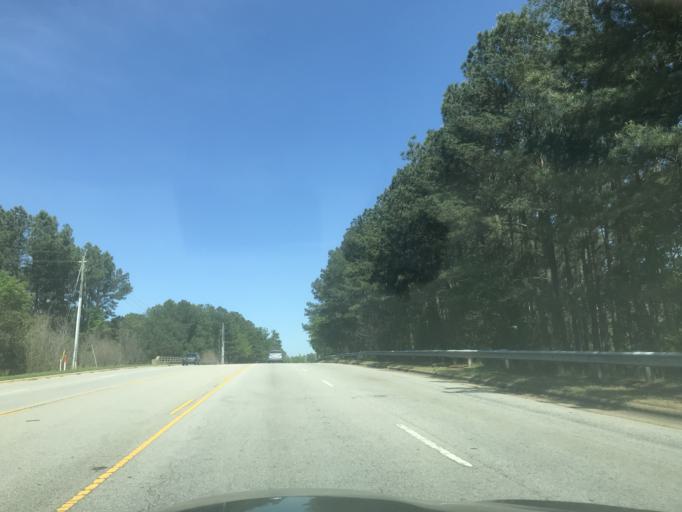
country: US
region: North Carolina
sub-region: Wake County
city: Garner
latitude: 35.7308
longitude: -78.6323
